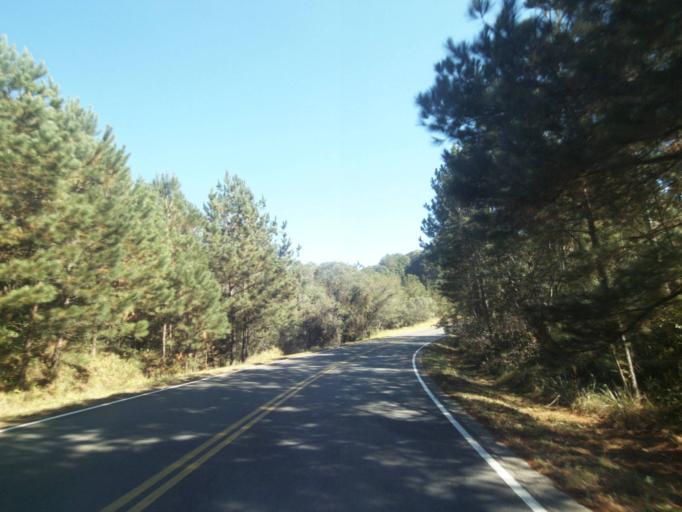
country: BR
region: Parana
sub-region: Telemaco Borba
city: Telemaco Borba
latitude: -24.4244
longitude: -50.5819
